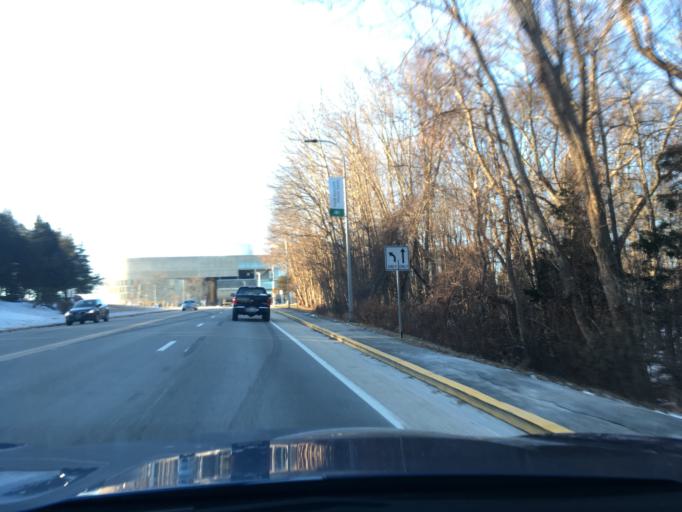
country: US
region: Rhode Island
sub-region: Kent County
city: West Warwick
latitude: 41.7152
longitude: -71.4802
